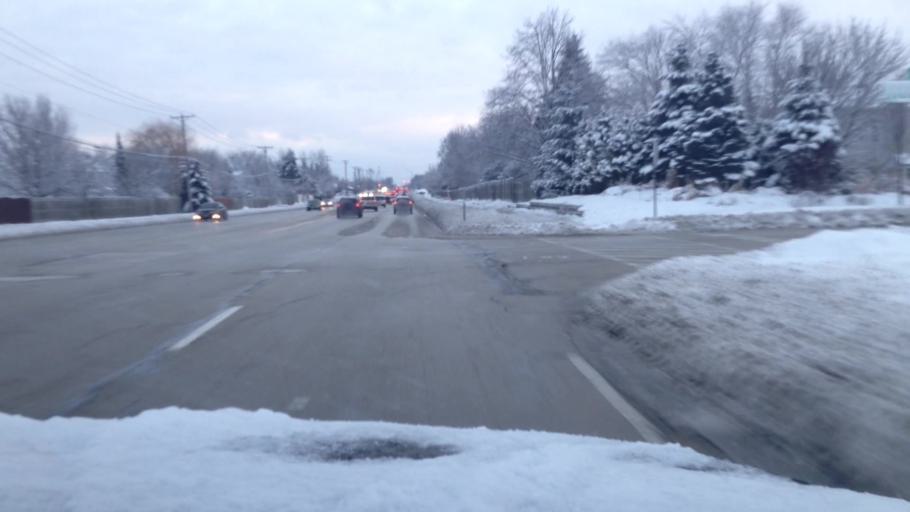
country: US
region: Illinois
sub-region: Kane County
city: South Elgin
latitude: 42.0030
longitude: -88.3156
